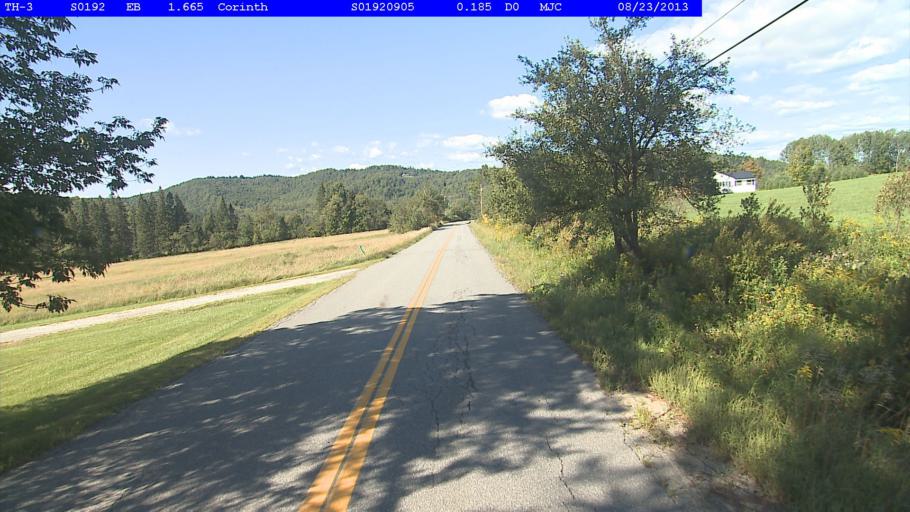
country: US
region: Vermont
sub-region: Orange County
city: Chelsea
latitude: 44.0046
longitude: -72.3509
